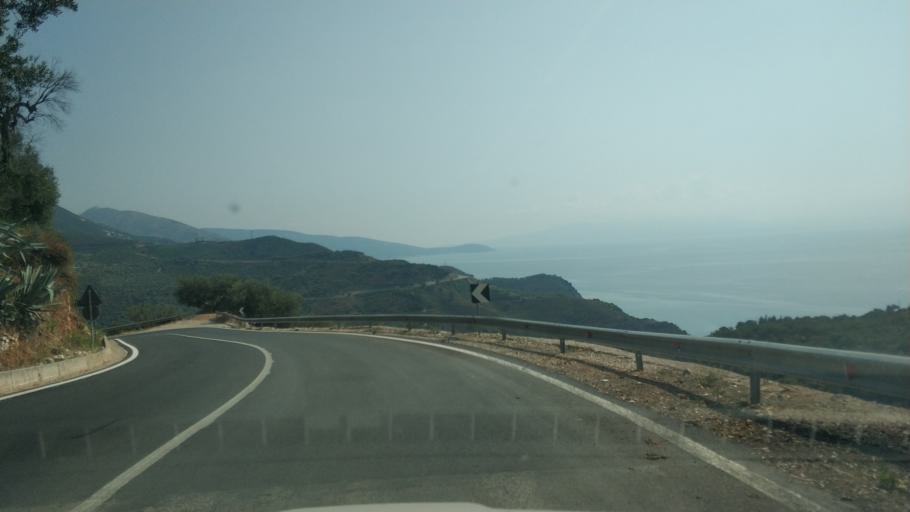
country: AL
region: Vlore
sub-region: Rrethi i Sarandes
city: Lukove
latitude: 40.0150
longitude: 19.8943
